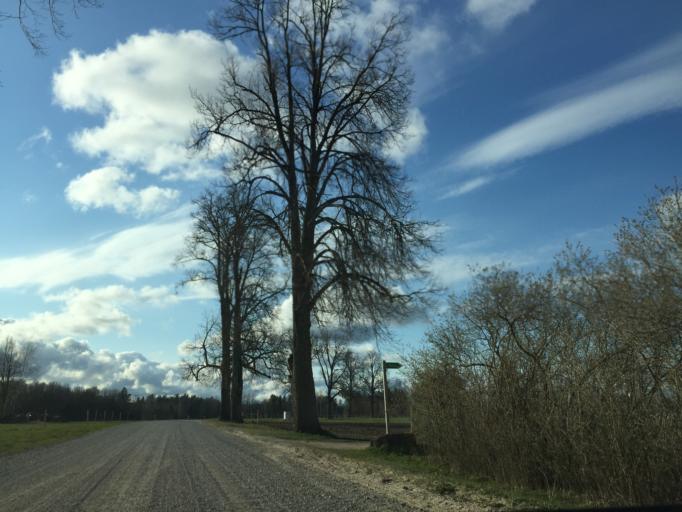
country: LV
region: Burtnieki
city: Matisi
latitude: 57.6046
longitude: 25.0806
